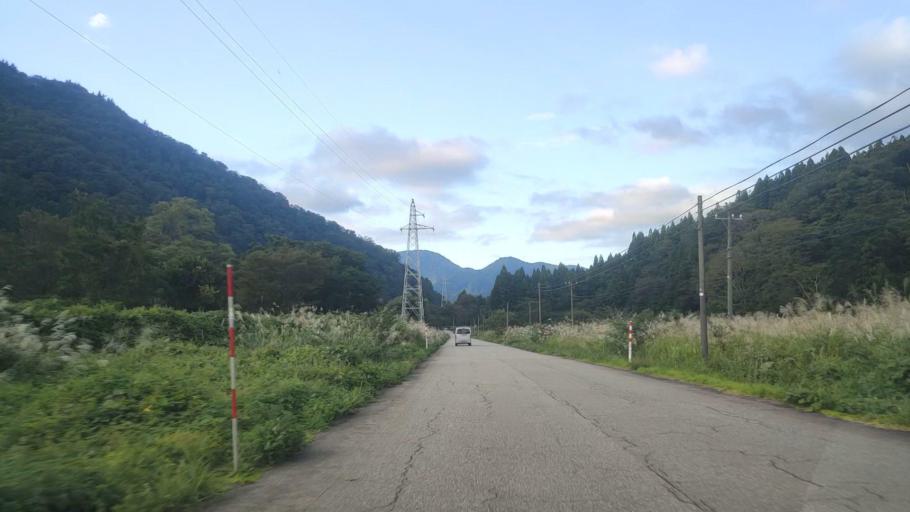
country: JP
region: Toyama
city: Yatsuomachi-higashikumisaka
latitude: 36.4571
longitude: 137.0846
